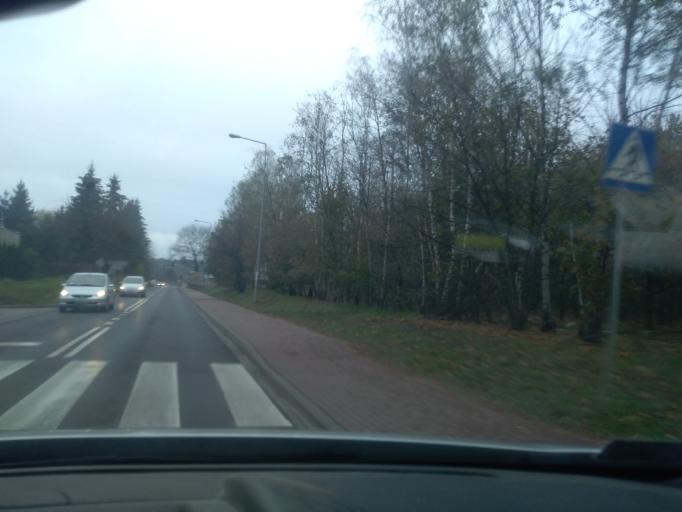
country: PL
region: Greater Poland Voivodeship
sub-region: Powiat poznanski
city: Murowana Goslina
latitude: 52.5411
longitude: 16.9688
